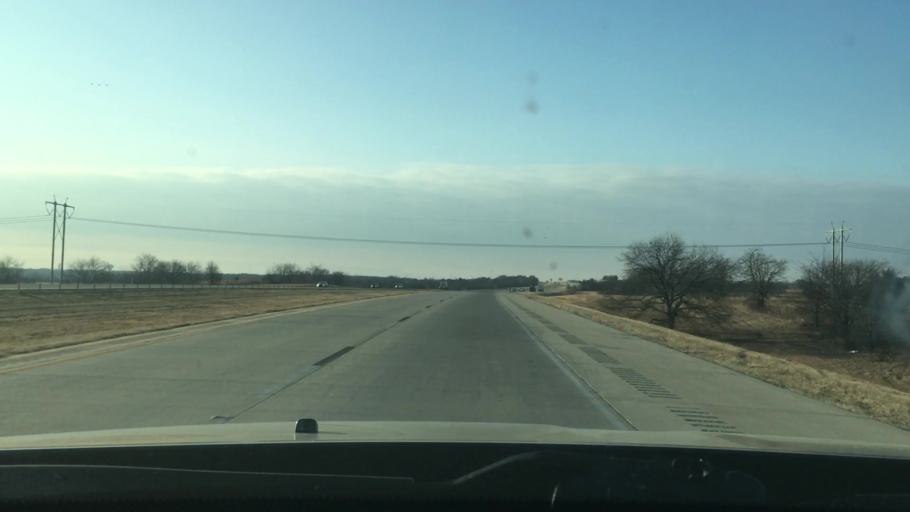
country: US
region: Oklahoma
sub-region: Carter County
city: Ardmore
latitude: 34.2341
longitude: -97.1617
